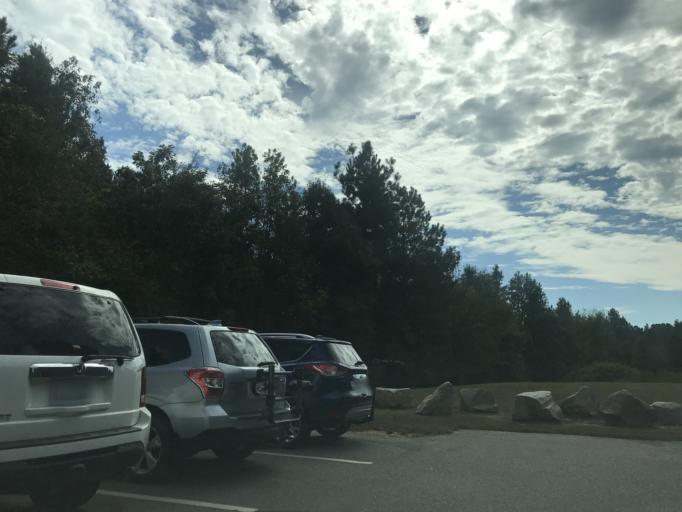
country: US
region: North Carolina
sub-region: Wake County
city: Rolesville
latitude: 35.8767
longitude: -78.5347
